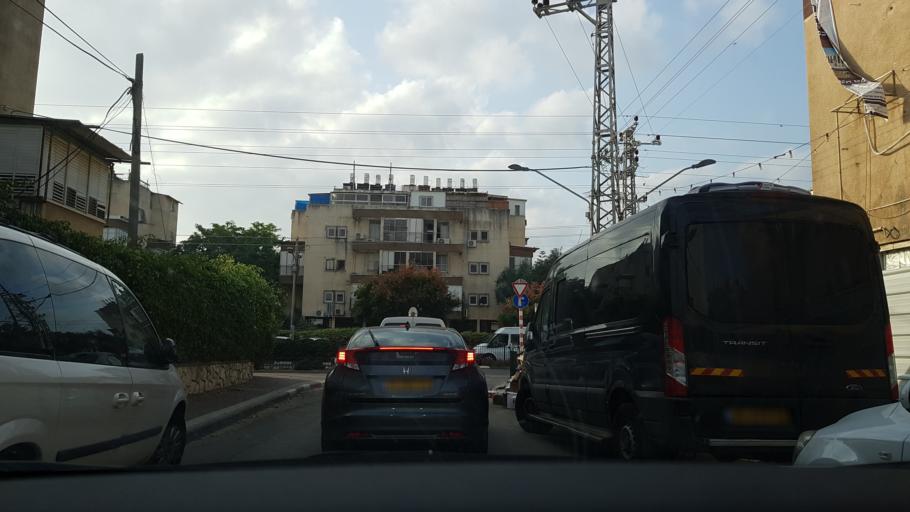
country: IL
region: Central District
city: Ness Ziona
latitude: 31.8940
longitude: 34.8244
